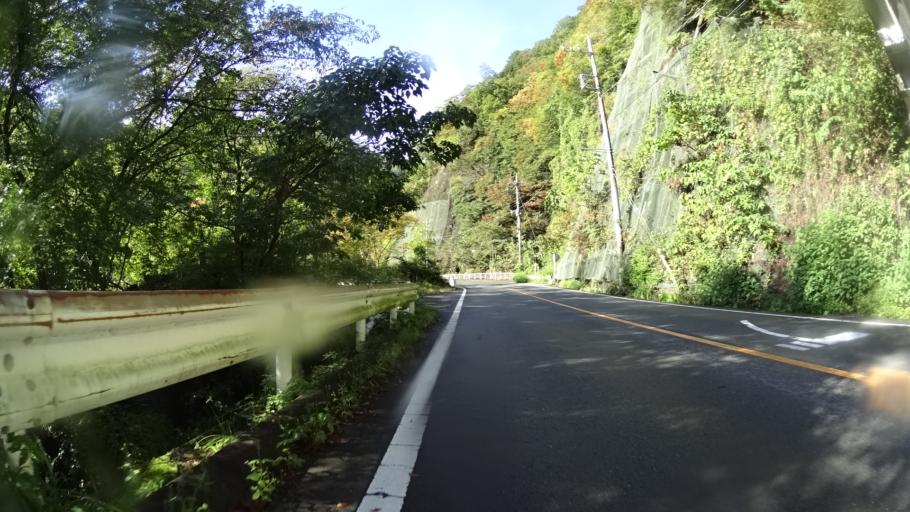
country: JP
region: Yamanashi
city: Otsuki
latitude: 35.7872
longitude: 138.9547
